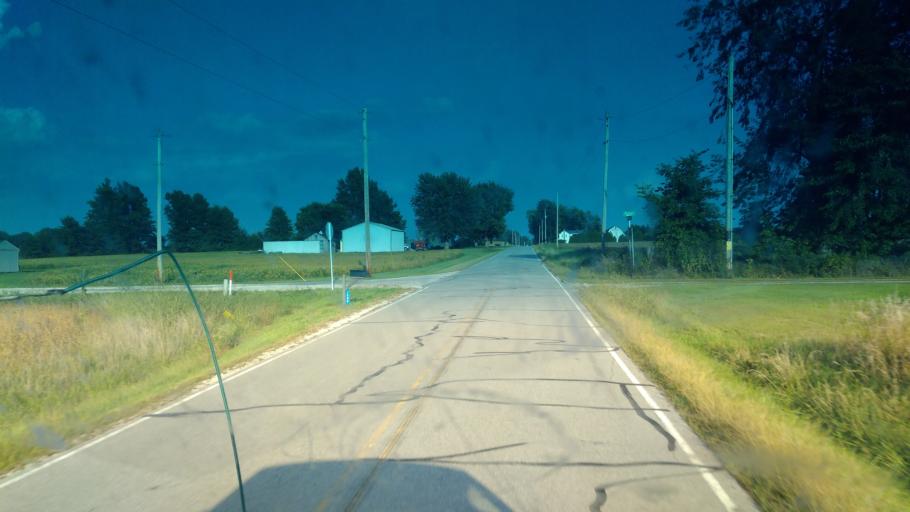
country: US
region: Ohio
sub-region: Crawford County
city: Bucyrus
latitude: 40.9650
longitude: -83.0360
